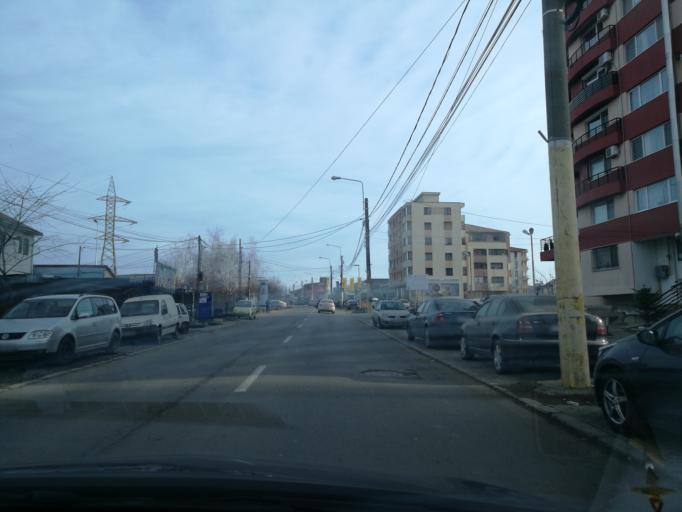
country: RO
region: Constanta
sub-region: Municipiul Constanta
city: Constanta
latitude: 44.1880
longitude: 28.6126
